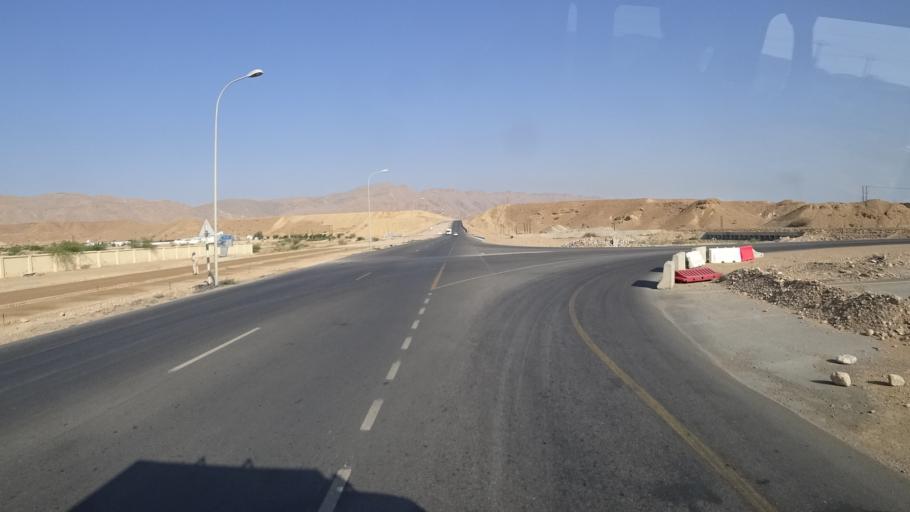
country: OM
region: Ash Sharqiyah
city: Sur
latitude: 22.5786
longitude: 59.4571
